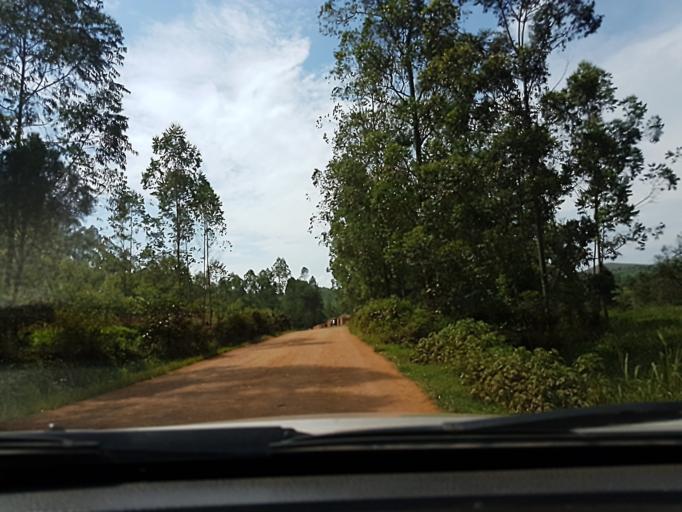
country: CD
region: South Kivu
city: Bukavu
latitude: -2.6391
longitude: 28.8754
